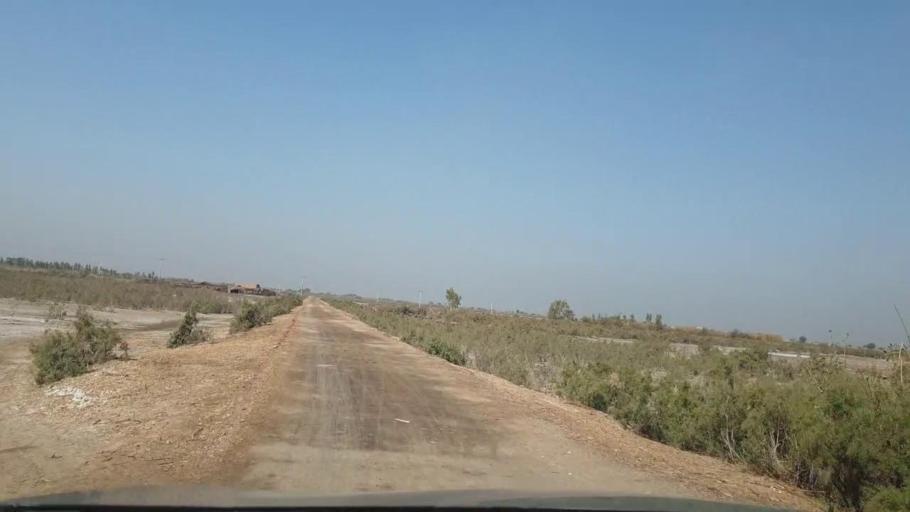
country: PK
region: Sindh
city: Berani
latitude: 25.6868
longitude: 68.8885
